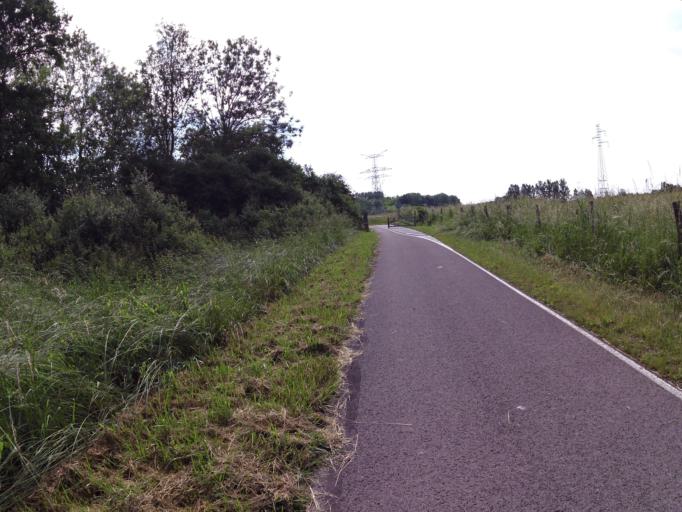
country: FR
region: Champagne-Ardenne
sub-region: Departement de l'Aube
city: Lusigny-sur-Barse
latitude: 48.2660
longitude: 4.2084
